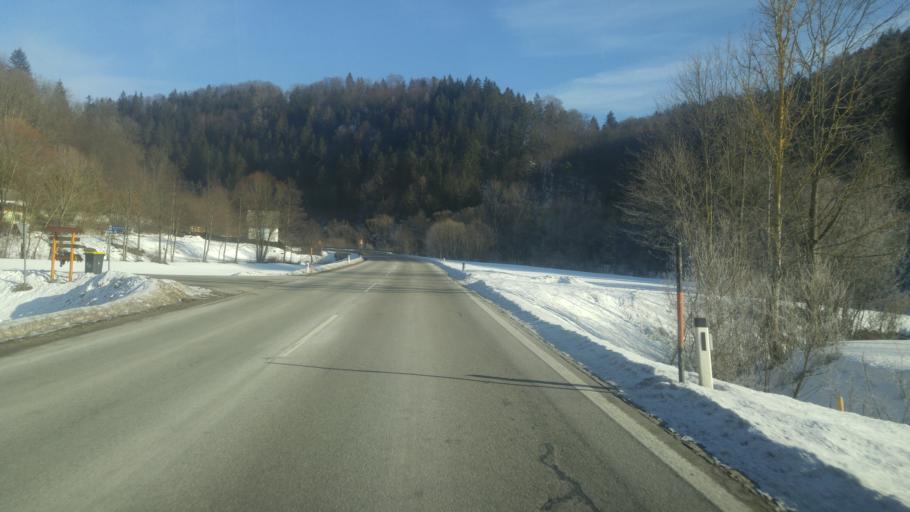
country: AT
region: Lower Austria
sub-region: Politischer Bezirk Lilienfeld
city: Turnitz
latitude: 47.9438
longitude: 15.5141
